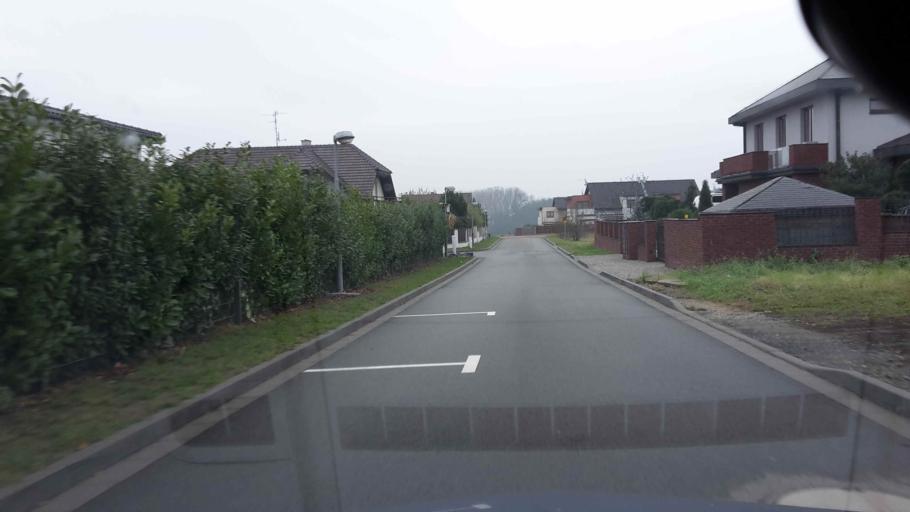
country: CZ
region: Olomoucky
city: Horka nad Moravou
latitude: 49.6115
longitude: 17.2059
